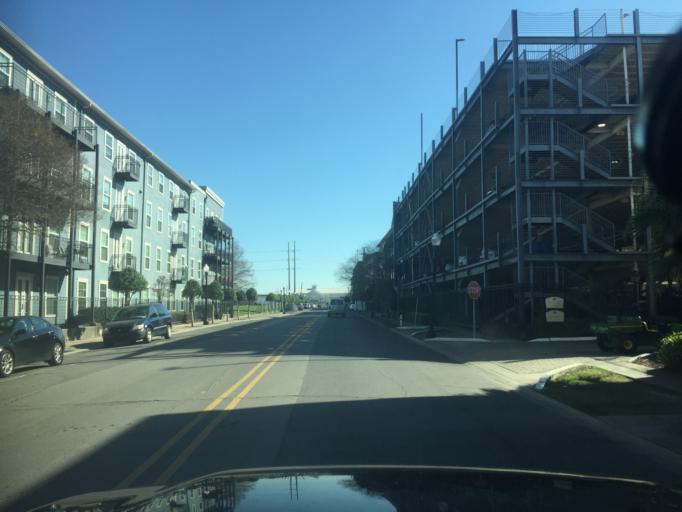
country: US
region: Louisiana
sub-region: Orleans Parish
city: New Orleans
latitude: 29.9347
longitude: -90.0693
